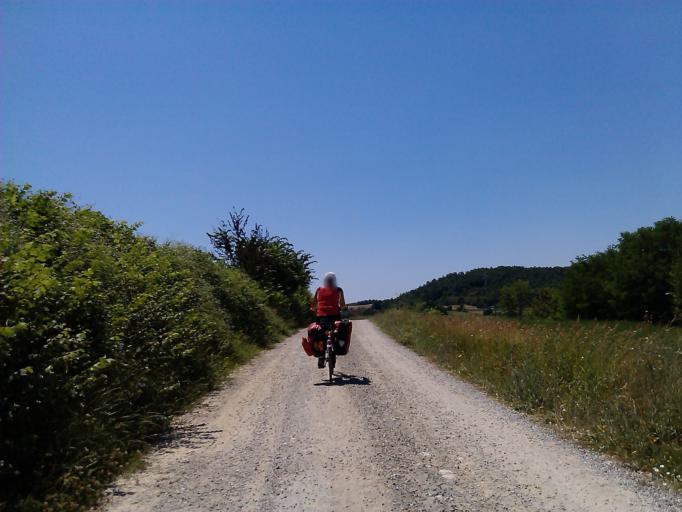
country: IT
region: Umbria
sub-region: Provincia di Terni
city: Fabro Scalo
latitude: 42.8522
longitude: 12.0408
